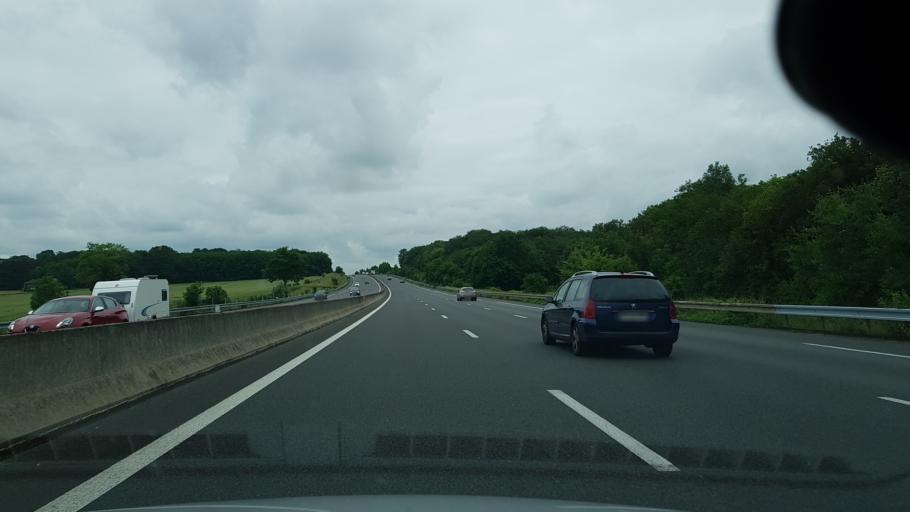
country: FR
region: Centre
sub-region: Departement du Loir-et-Cher
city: Saint-Sulpice-de-Pommeray
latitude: 47.6197
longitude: 1.2370
